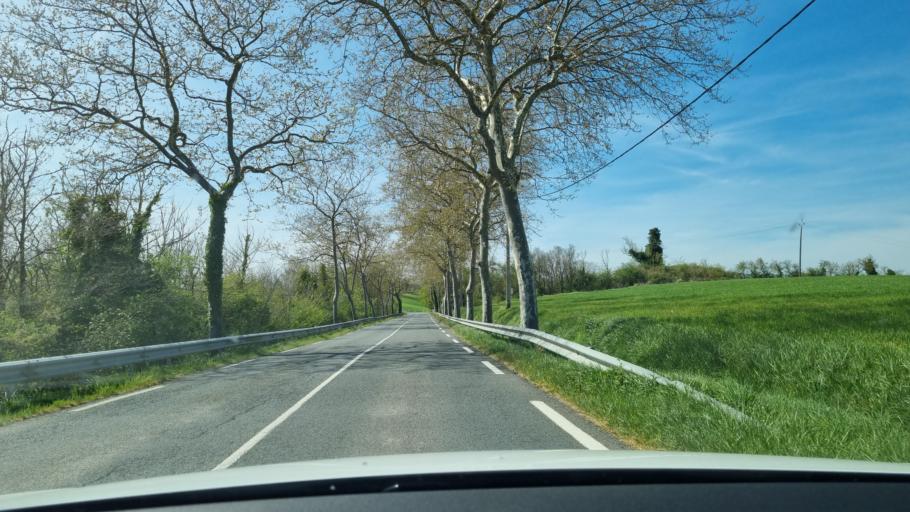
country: FR
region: Midi-Pyrenees
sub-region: Departement de la Haute-Garonne
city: Sainte-Foy-de-Peyrolieres
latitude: 43.4863
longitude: 1.0542
